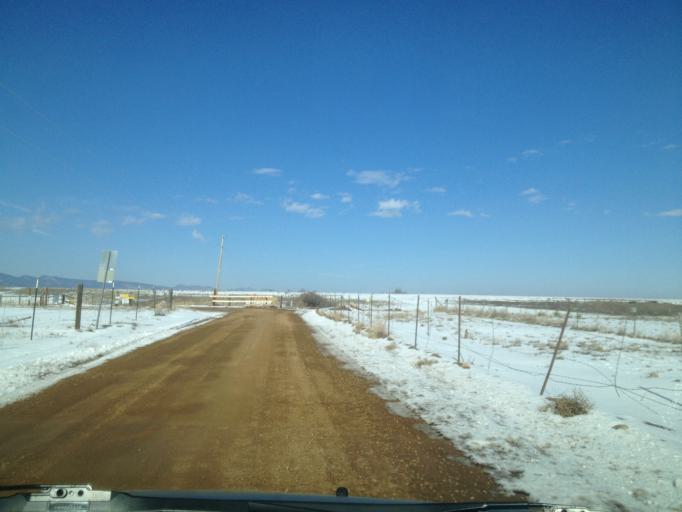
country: US
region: Colorado
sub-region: Boulder County
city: Boulder
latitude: 40.0631
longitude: -105.2633
